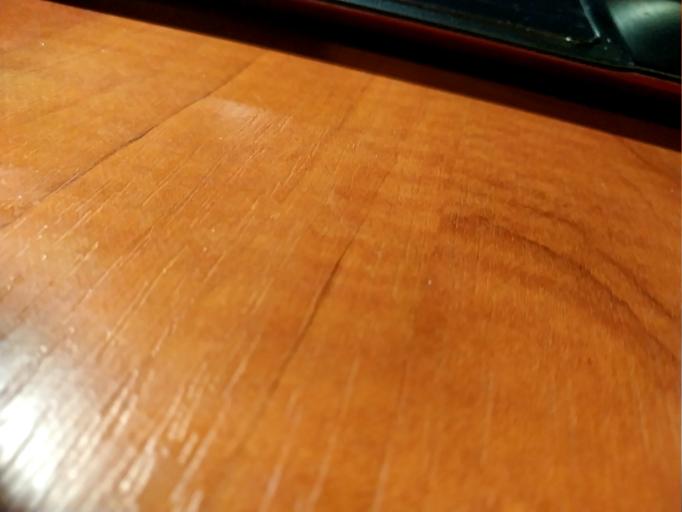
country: RU
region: Tverskaya
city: Ves'yegonsk
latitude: 58.7247
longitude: 37.5439
